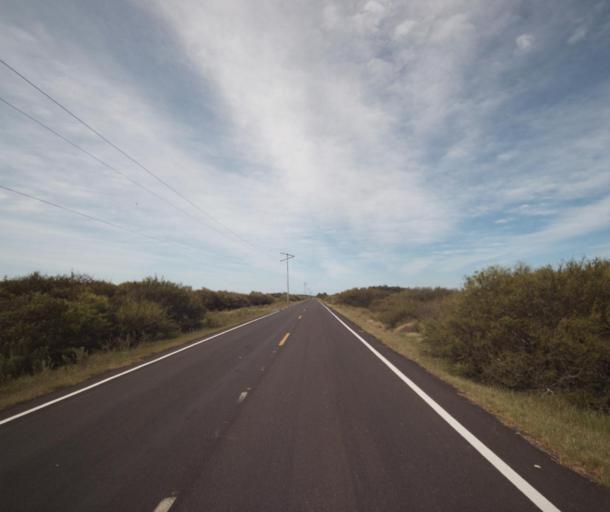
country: BR
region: Rio Grande do Sul
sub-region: Rio Grande
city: Rio Grande
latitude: -31.9121
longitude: -51.9364
